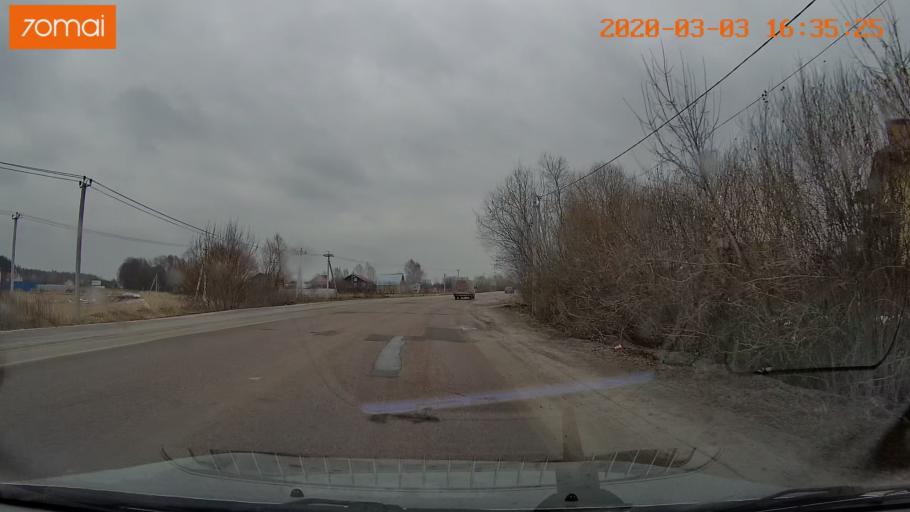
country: RU
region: Moskovskaya
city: Lopatinskiy
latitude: 55.4046
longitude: 38.7643
